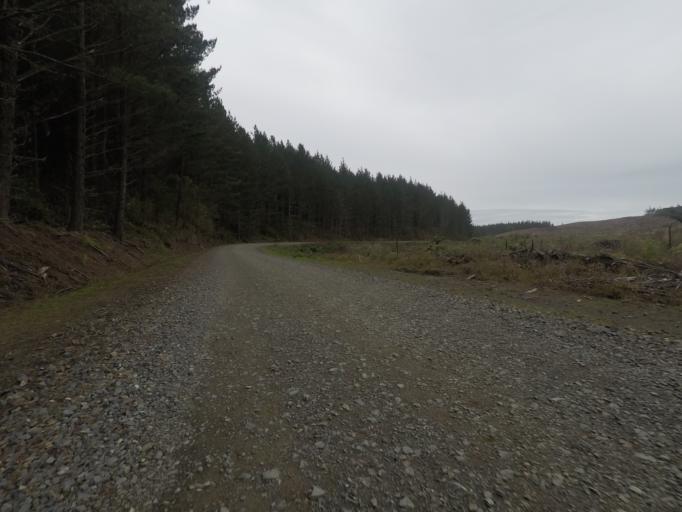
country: NZ
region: Auckland
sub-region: Auckland
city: Muriwai Beach
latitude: -36.7475
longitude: 174.5758
